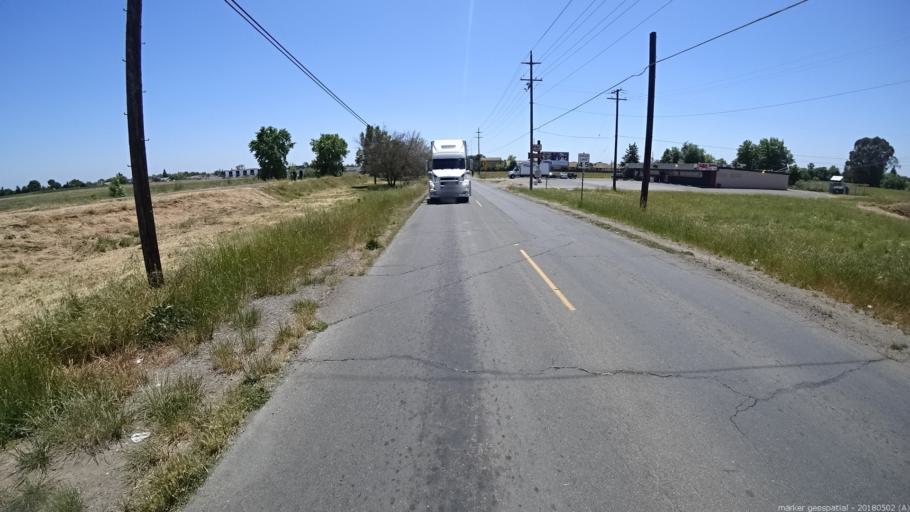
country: US
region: California
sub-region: Sacramento County
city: Rio Linda
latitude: 38.6548
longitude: -121.4478
